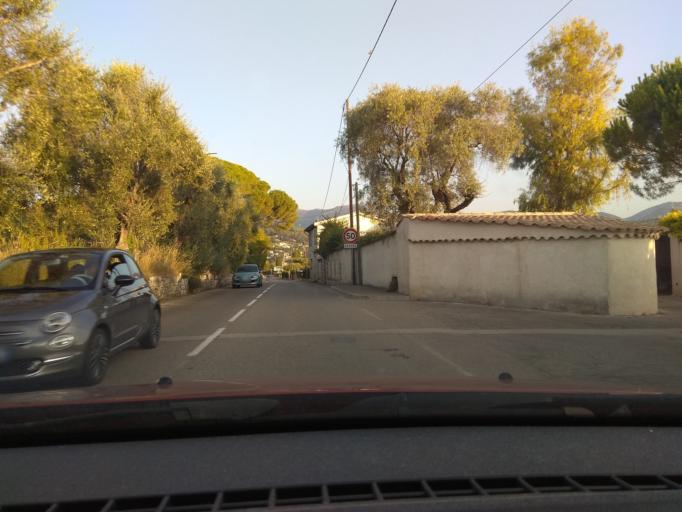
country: FR
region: Provence-Alpes-Cote d'Azur
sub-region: Departement des Alpes-Maritimes
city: La Colle-sur-Loup
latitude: 43.6820
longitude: 7.1133
